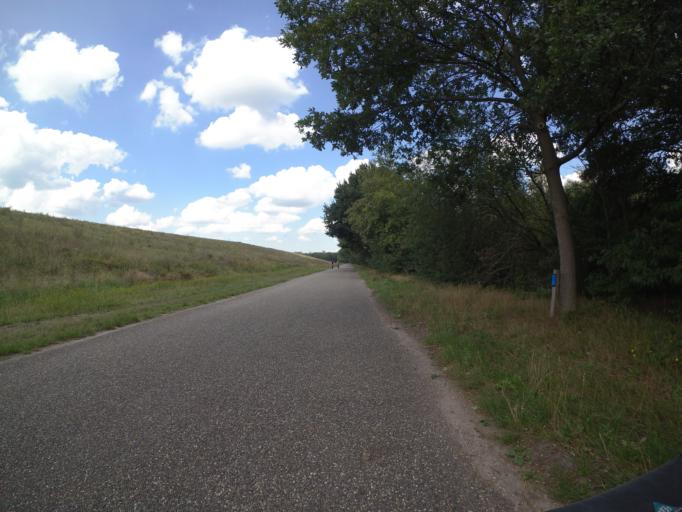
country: NL
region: North Brabant
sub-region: Gemeente Veghel
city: Eerde
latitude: 51.5955
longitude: 5.4901
